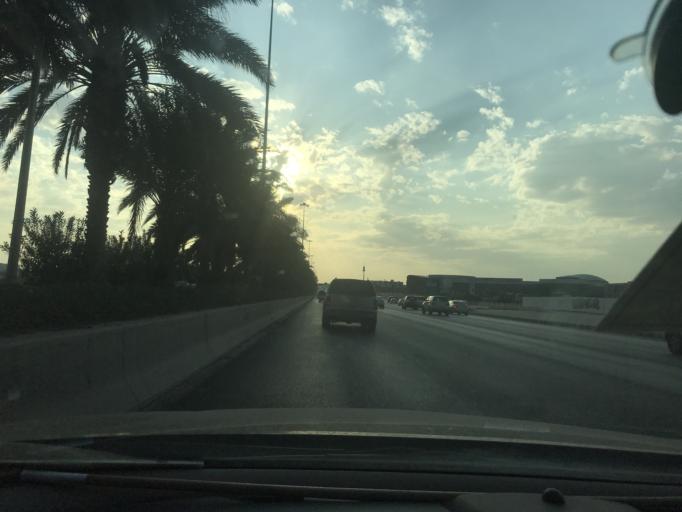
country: SA
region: Ar Riyad
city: Riyadh
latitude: 24.7563
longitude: 46.6360
